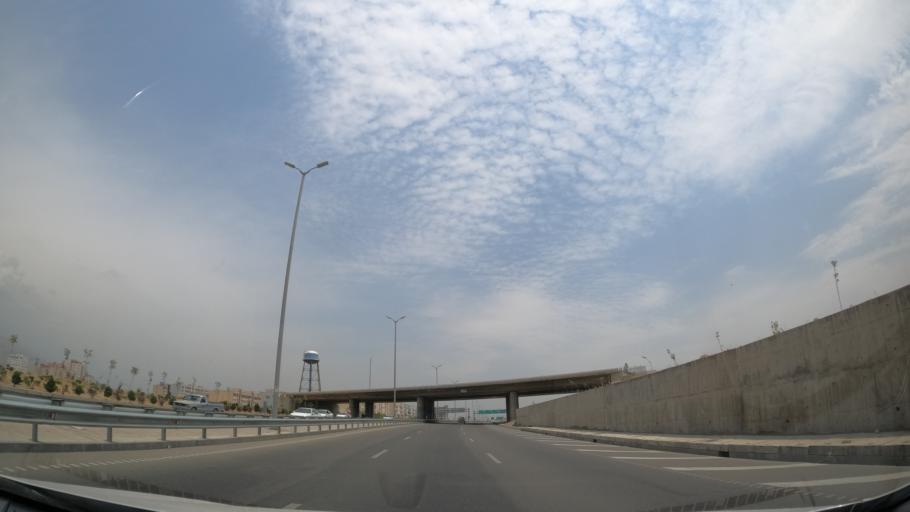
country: IR
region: Tehran
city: Shahr-e Qods
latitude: 35.7413
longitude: 51.2445
